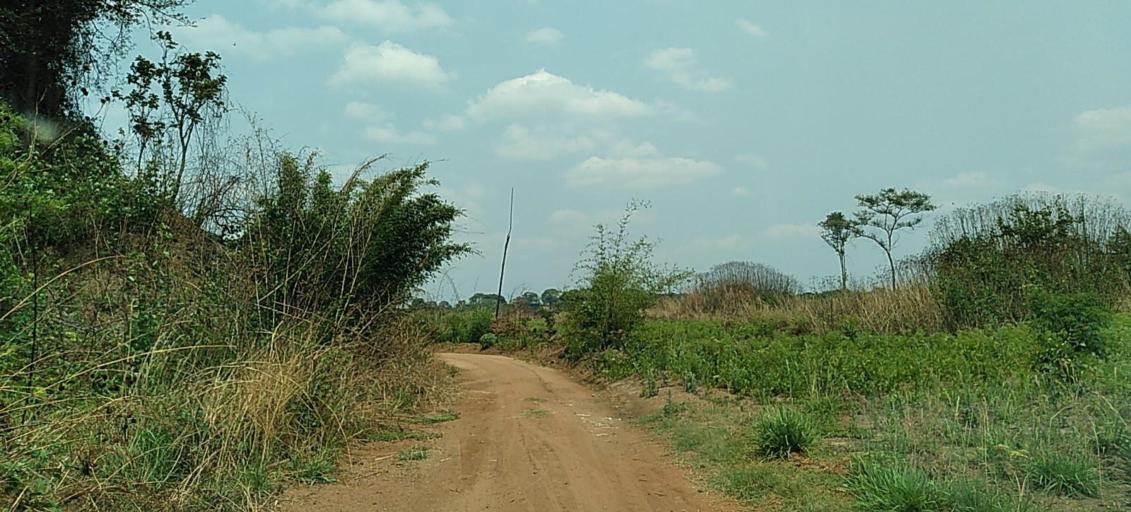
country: ZM
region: Copperbelt
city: Kalulushi
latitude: -12.7586
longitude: 28.0230
